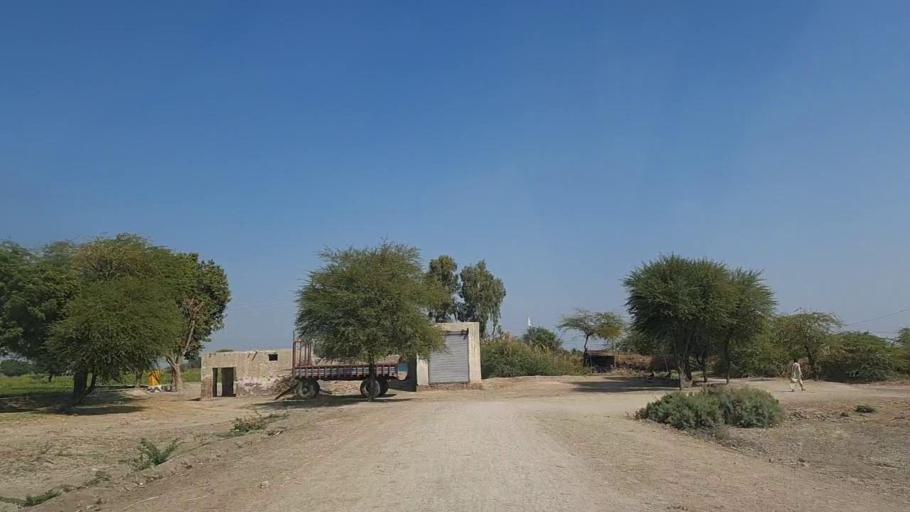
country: PK
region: Sindh
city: Digri
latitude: 25.2055
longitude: 69.1449
